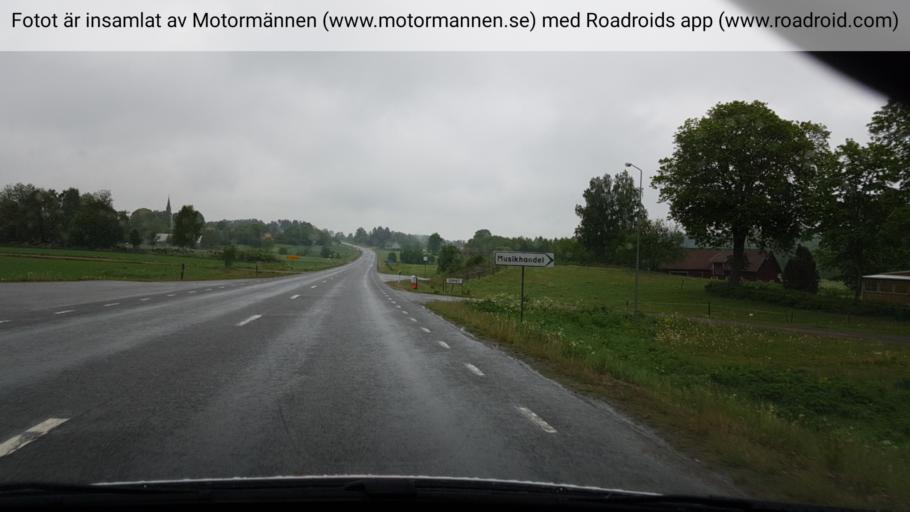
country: SE
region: Vaestra Goetaland
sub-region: Ulricehamns Kommun
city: Ulricehamn
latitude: 57.9525
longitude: 13.5178
